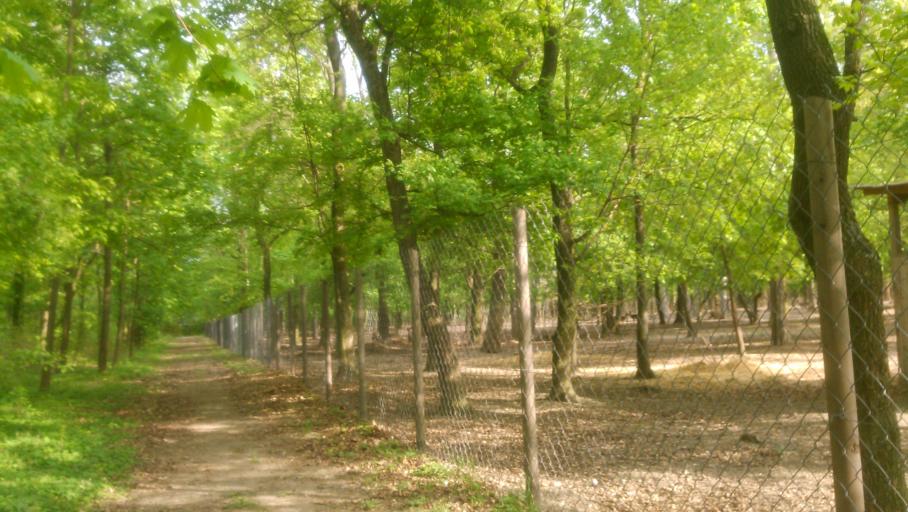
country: SK
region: Bratislavsky
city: Dunajska Luzna
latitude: 48.1373
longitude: 17.3241
